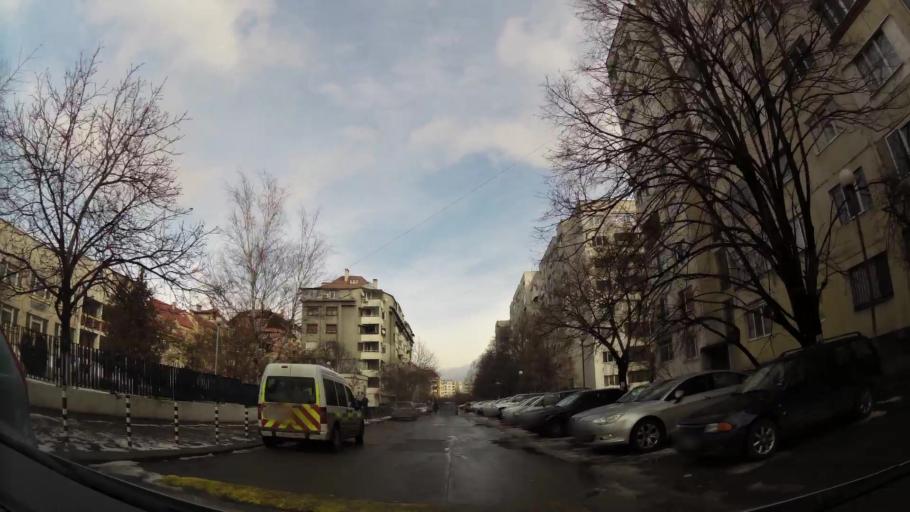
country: BG
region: Sofia-Capital
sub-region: Stolichna Obshtina
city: Sofia
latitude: 42.7143
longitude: 23.2704
